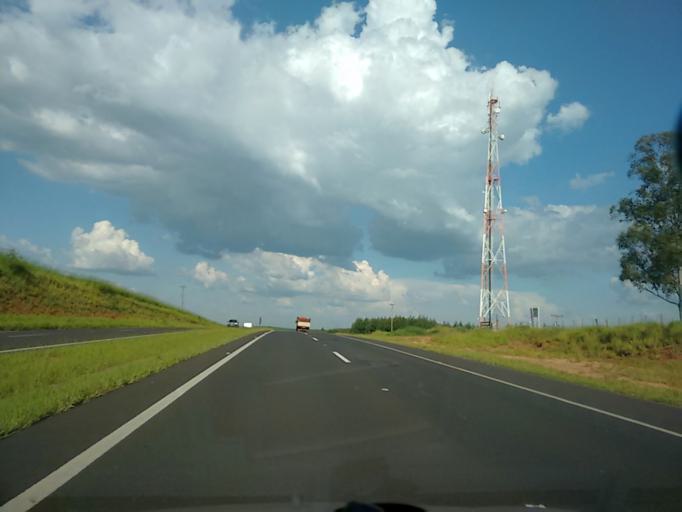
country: BR
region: Sao Paulo
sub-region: Duartina
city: Duartina
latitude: -22.3247
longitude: -49.4201
